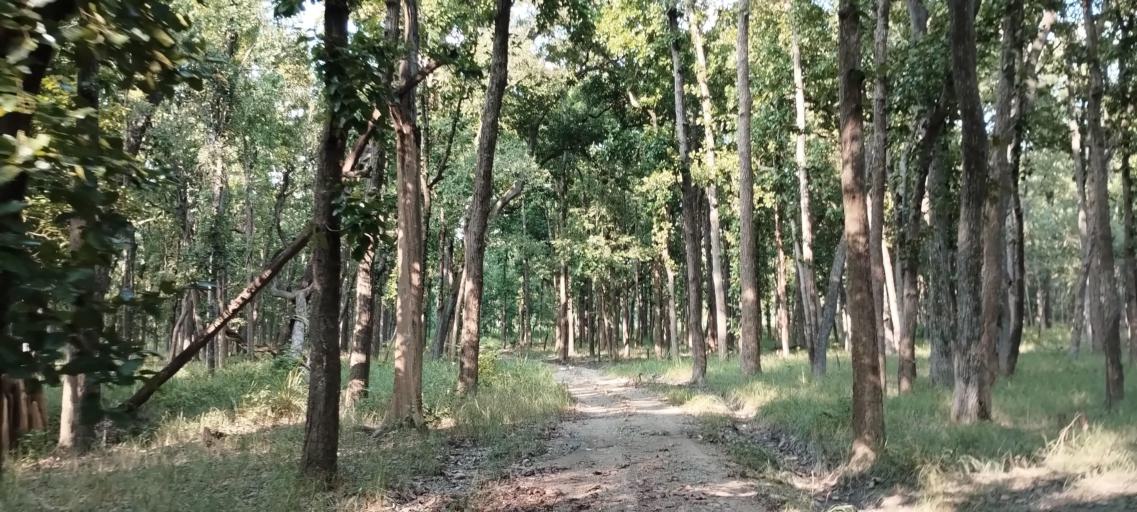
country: NP
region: Far Western
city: Tikapur
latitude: 28.5193
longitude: 81.2827
